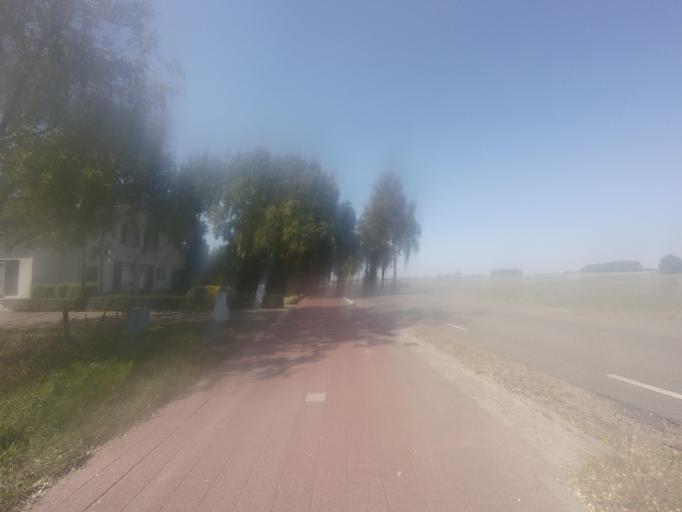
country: NL
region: North Brabant
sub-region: Gemeente Goirle
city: Goirle
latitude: 51.5120
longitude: 5.0872
